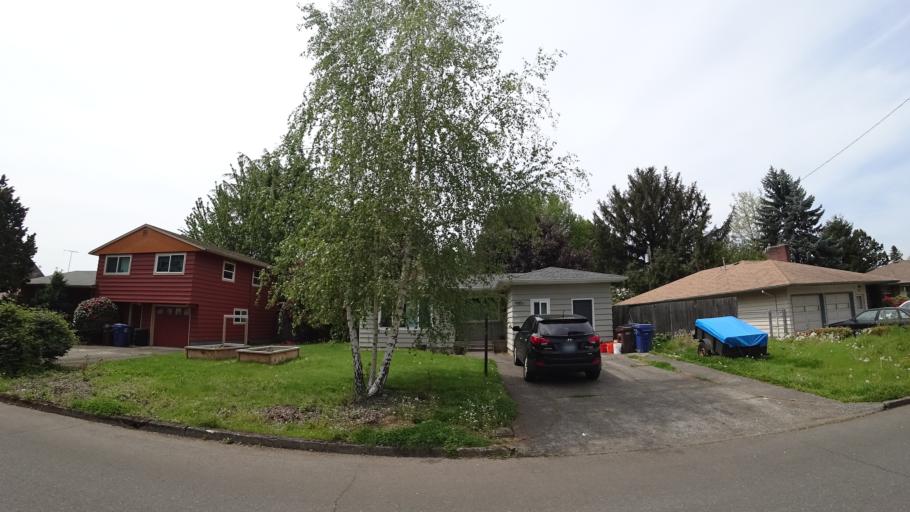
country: US
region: Oregon
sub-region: Clackamas County
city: Milwaukie
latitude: 45.4514
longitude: -122.6126
